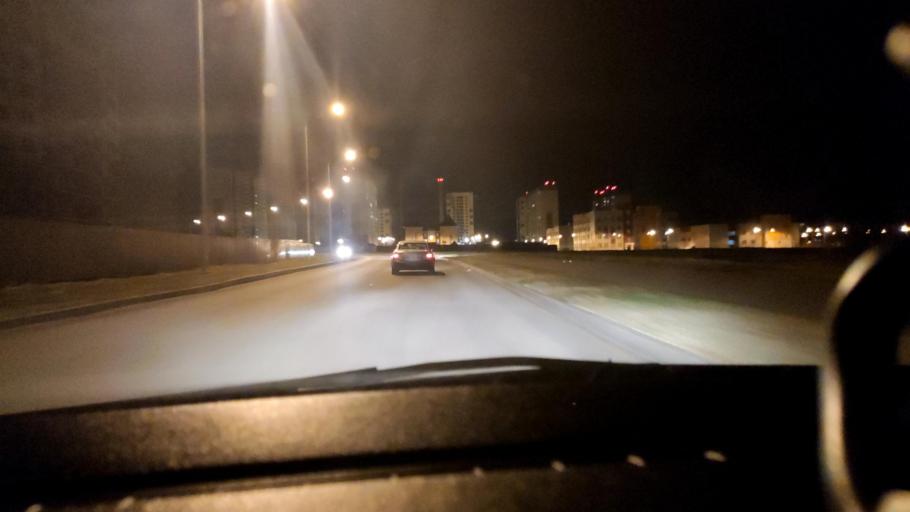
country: RU
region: Voronezj
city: Shilovo
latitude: 51.5709
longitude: 39.1212
